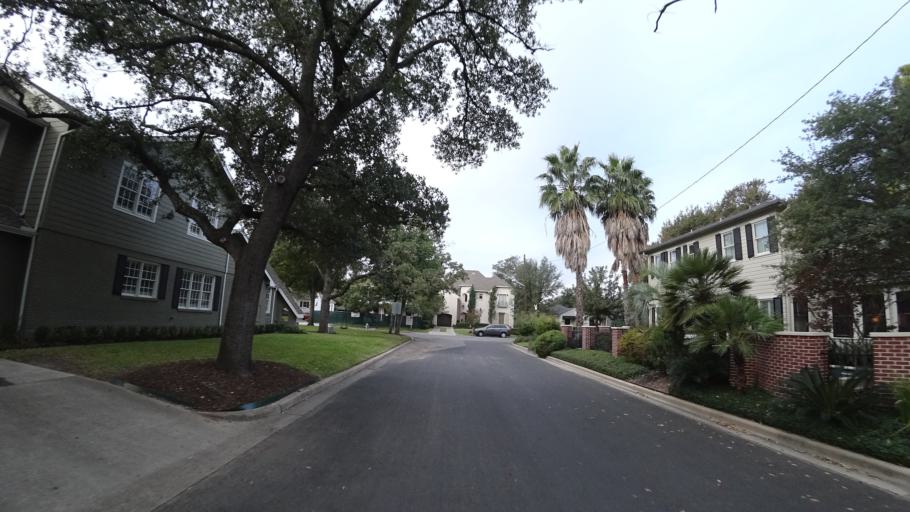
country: US
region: Texas
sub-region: Travis County
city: Austin
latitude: 30.2989
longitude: -97.7549
